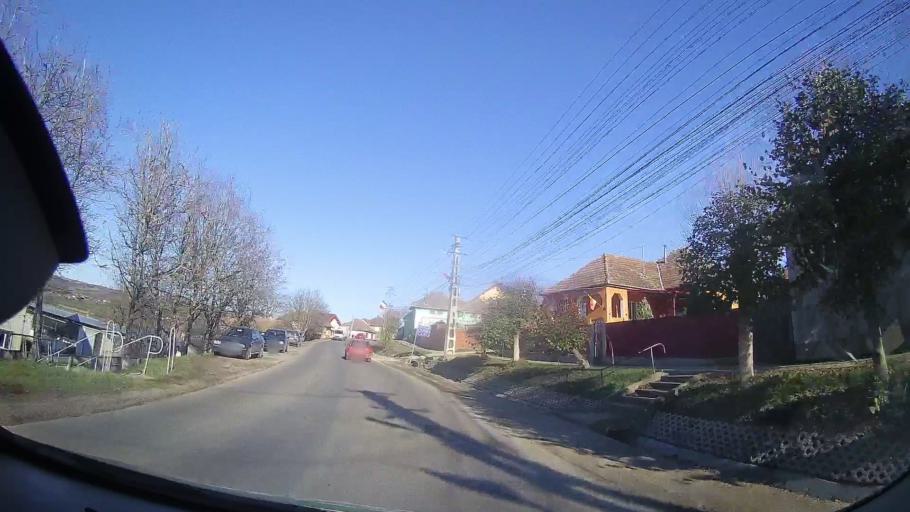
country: RO
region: Mures
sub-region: Comuna Sarmasu
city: Sarmasu
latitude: 46.7490
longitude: 24.1537
